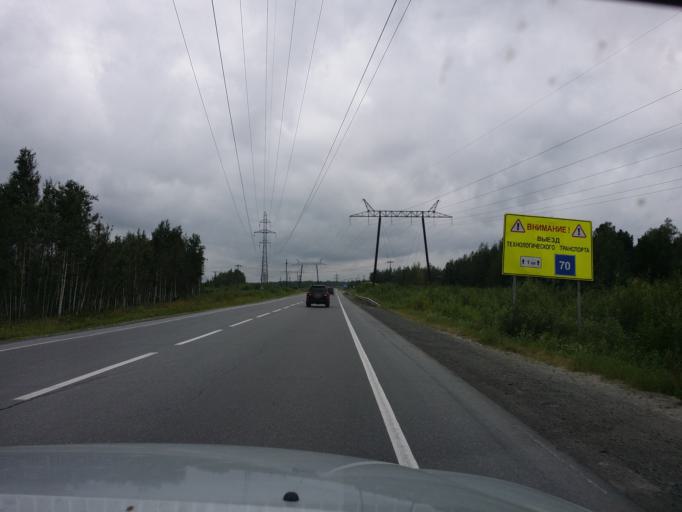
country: RU
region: Khanty-Mansiyskiy Avtonomnyy Okrug
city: Nizhnevartovsk
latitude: 61.0370
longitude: 76.3566
